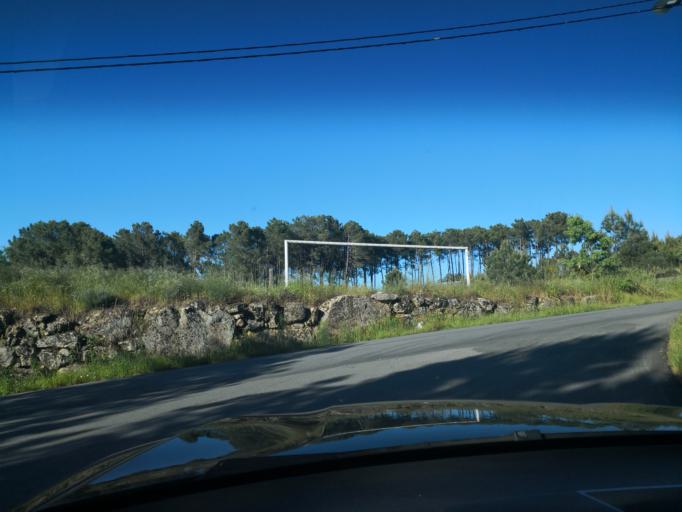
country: PT
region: Vila Real
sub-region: Vila Real
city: Vila Real
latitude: 41.3154
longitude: -7.6992
